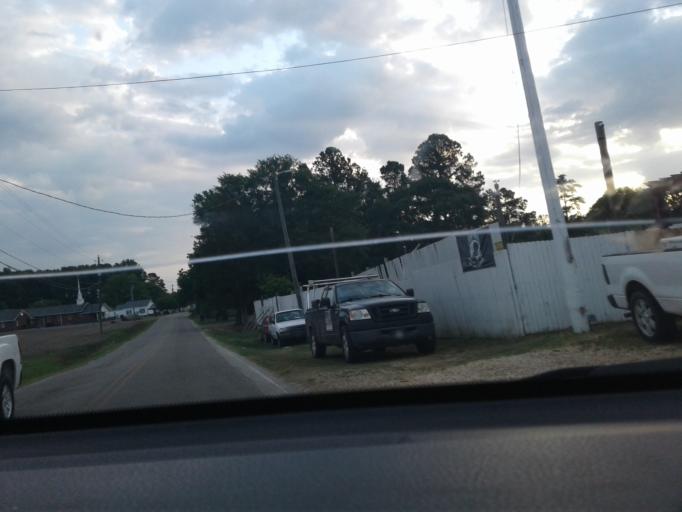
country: US
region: North Carolina
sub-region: Harnett County
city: Erwin
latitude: 35.3232
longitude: -78.6517
